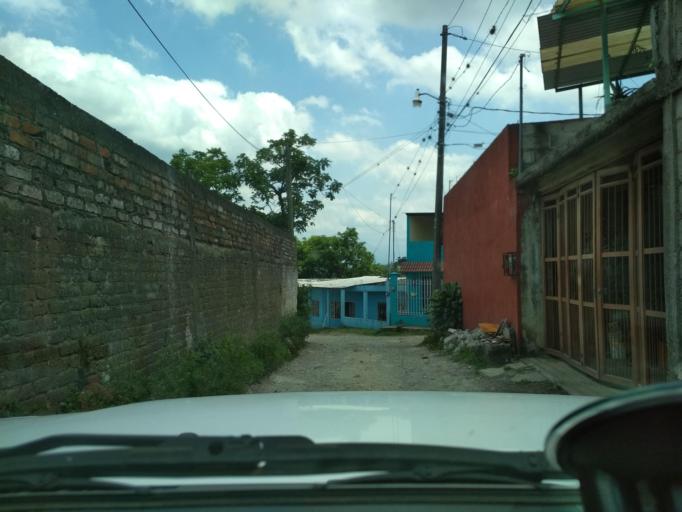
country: MX
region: Veracruz
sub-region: Fortin
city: Monte Salas
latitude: 18.9340
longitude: -97.0166
